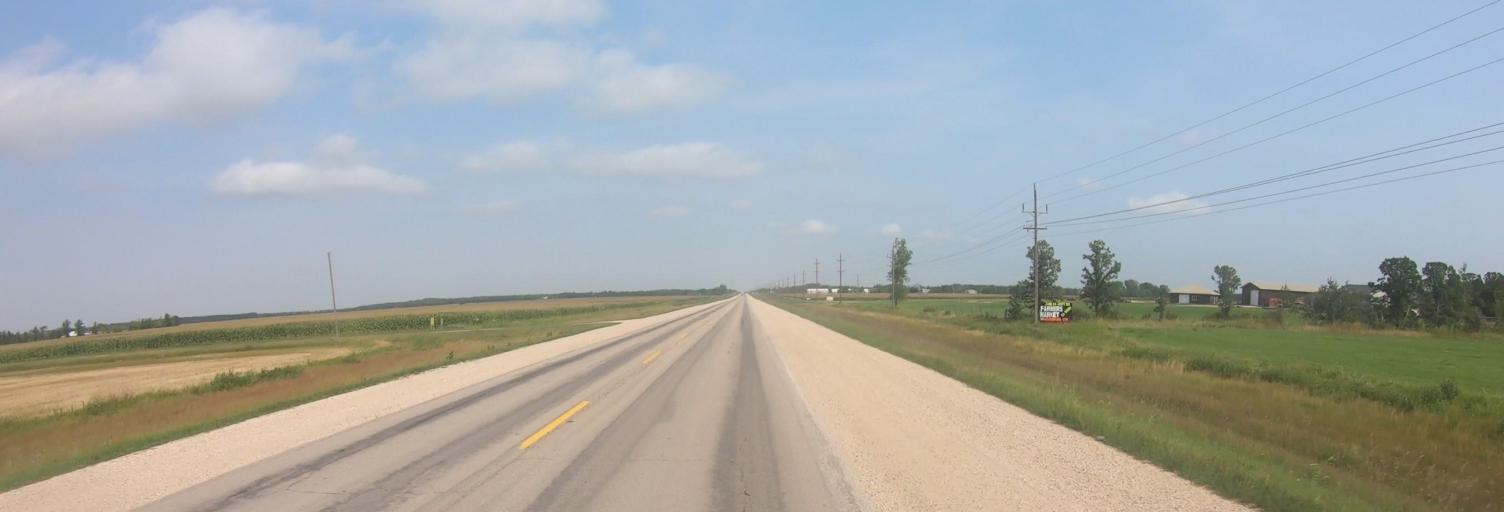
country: CA
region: Manitoba
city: Steinbach
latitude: 49.4655
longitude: -96.6907
